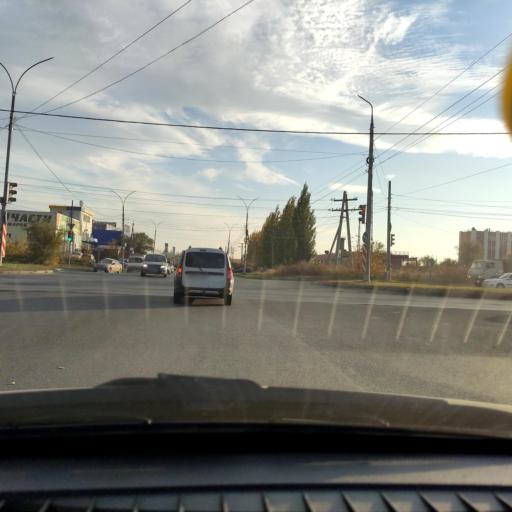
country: RU
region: Samara
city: Tol'yatti
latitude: 53.5610
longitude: 49.2951
